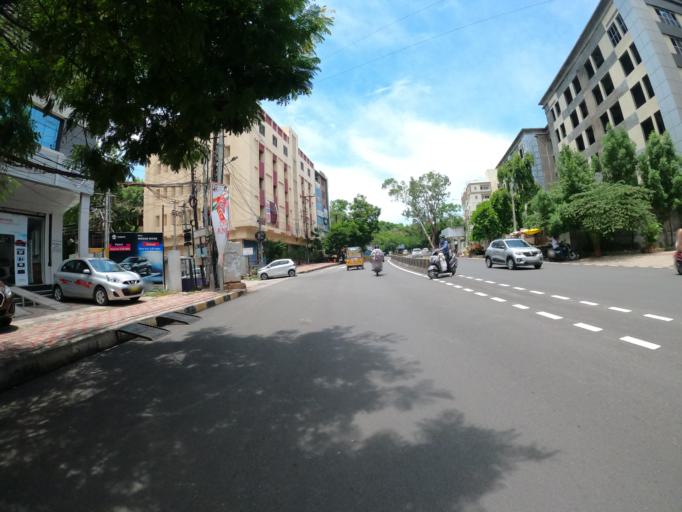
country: IN
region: Telangana
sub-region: Hyderabad
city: Hyderabad
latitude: 17.3970
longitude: 78.4844
